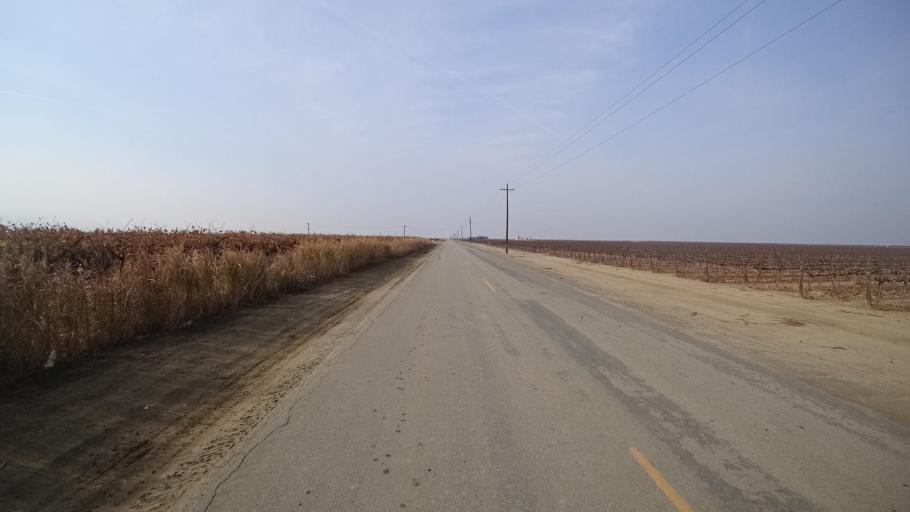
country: US
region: California
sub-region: Kern County
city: Greenfield
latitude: 35.0767
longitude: -119.0858
